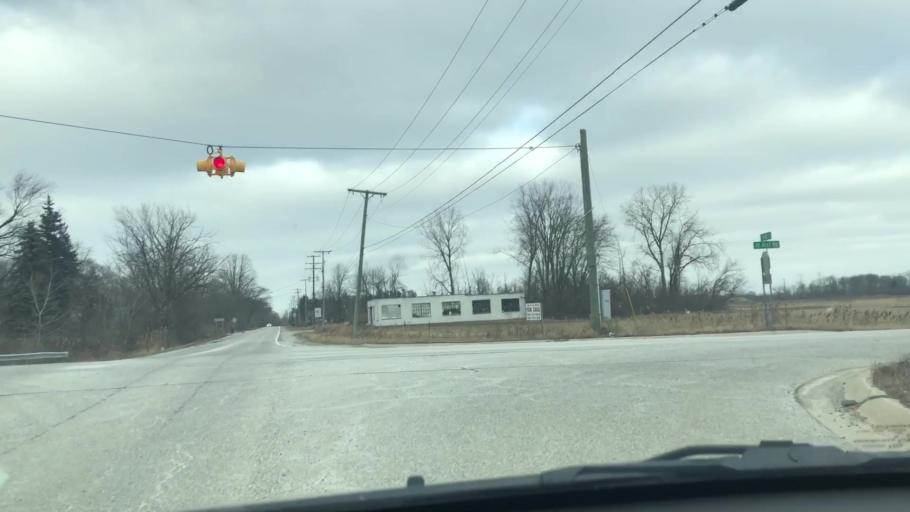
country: US
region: Michigan
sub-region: Macomb County
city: Romeo
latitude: 42.7433
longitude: -83.0174
